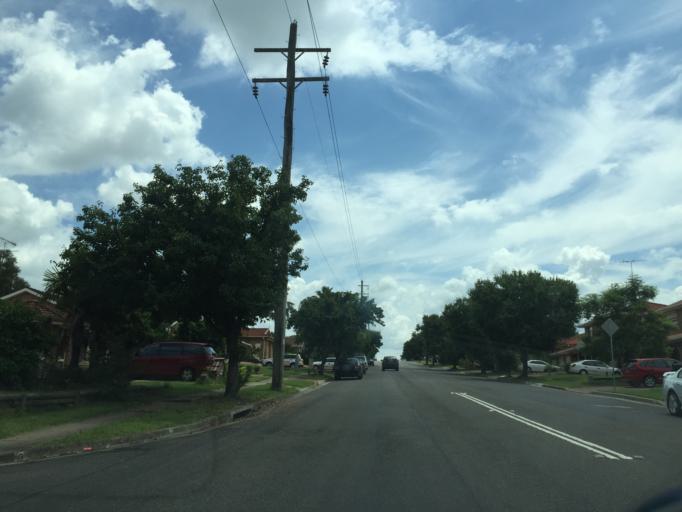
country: AU
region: New South Wales
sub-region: Blacktown
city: Quakers Hill
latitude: -33.7114
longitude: 150.8855
